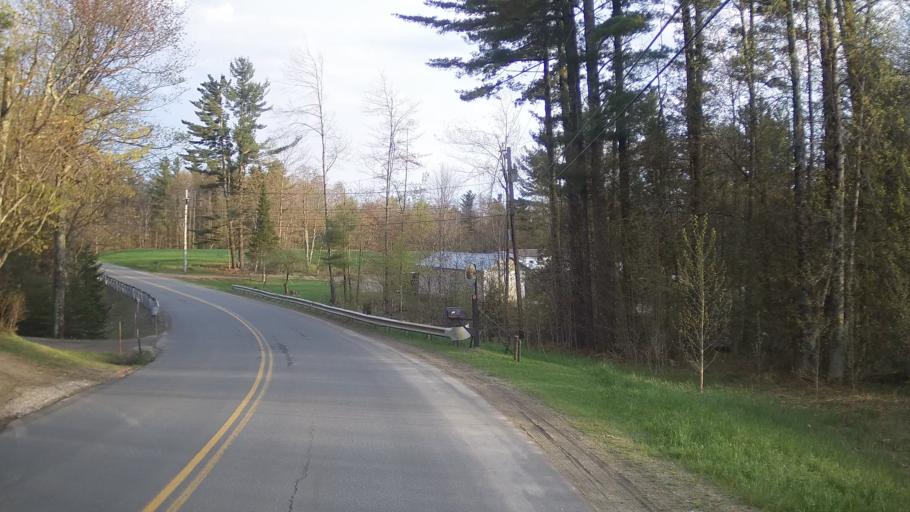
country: US
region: Vermont
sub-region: Orleans County
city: Newport
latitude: 44.8943
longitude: -72.4314
